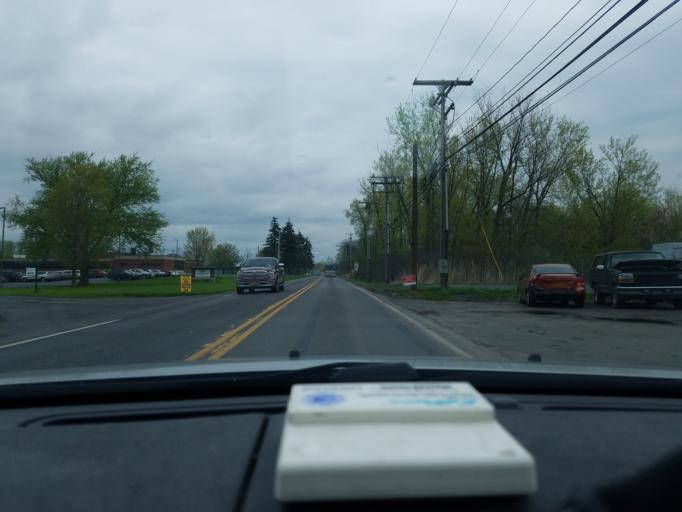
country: US
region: New York
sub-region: Onondaga County
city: East Syracuse
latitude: 43.0844
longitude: -76.0976
